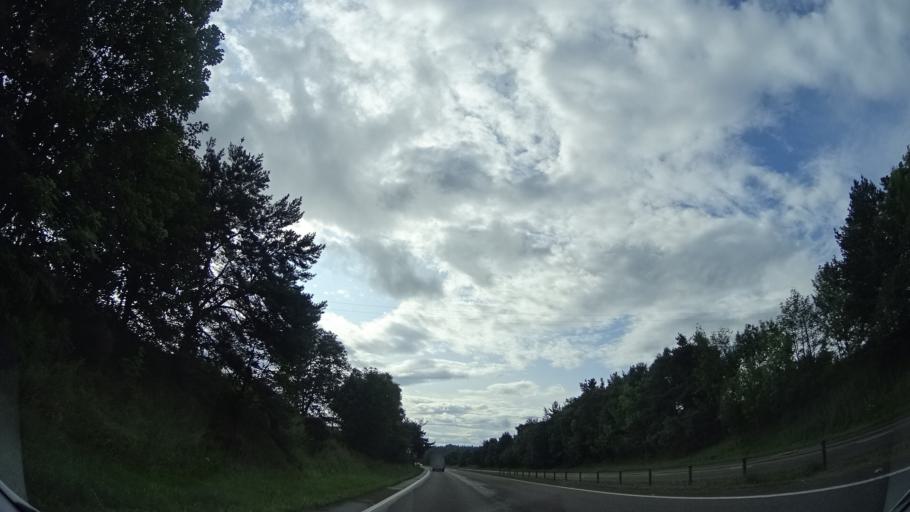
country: GB
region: Scotland
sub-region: Highland
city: Inverness
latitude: 57.5250
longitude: -4.3203
